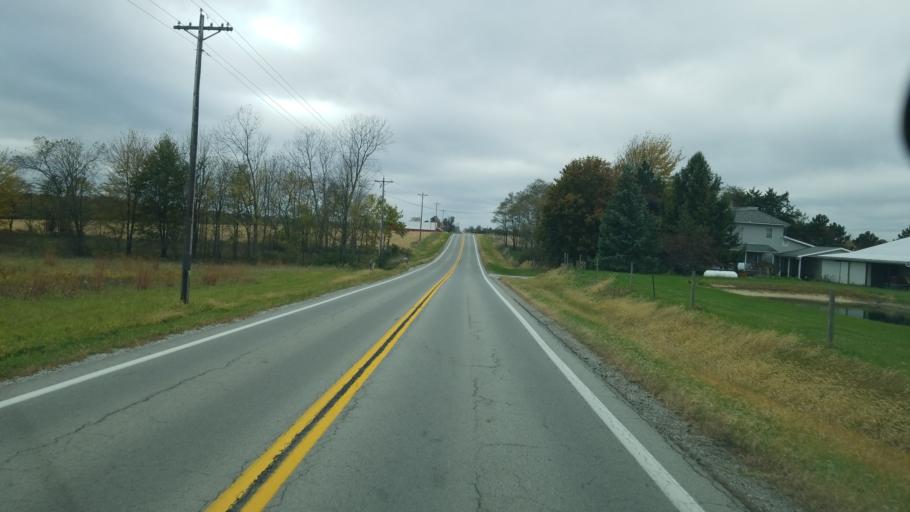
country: US
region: Ohio
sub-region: Sandusky County
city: Mount Carmel
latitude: 41.0812
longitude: -82.9675
